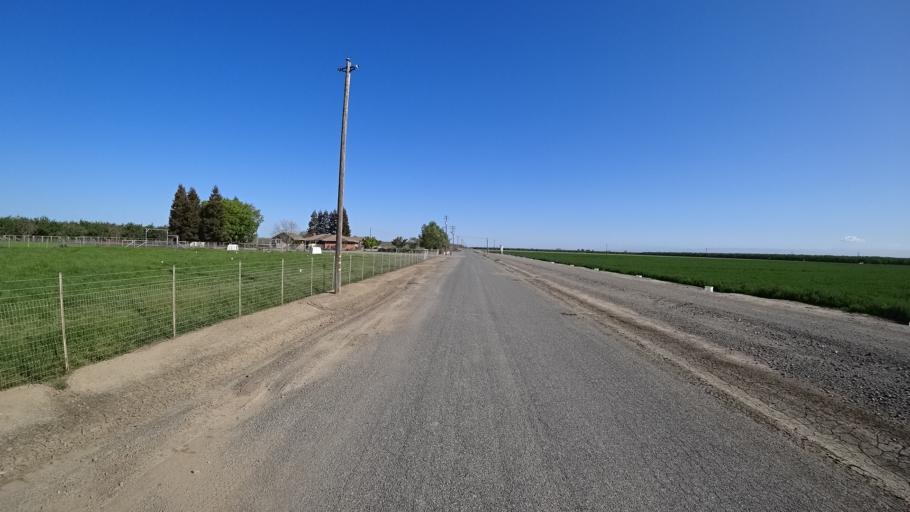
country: US
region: California
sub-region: Glenn County
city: Hamilton City
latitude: 39.6790
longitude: -122.0641
